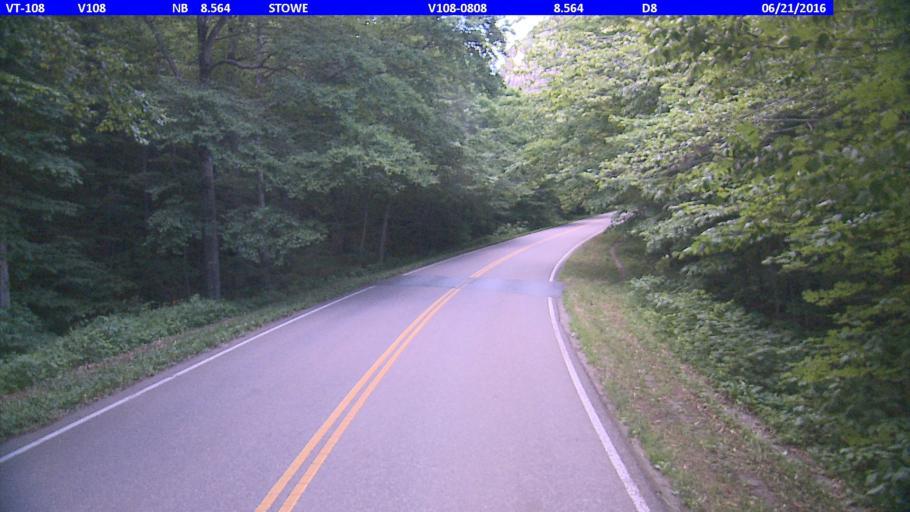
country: US
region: Vermont
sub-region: Lamoille County
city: Johnson
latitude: 44.5418
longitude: -72.7925
